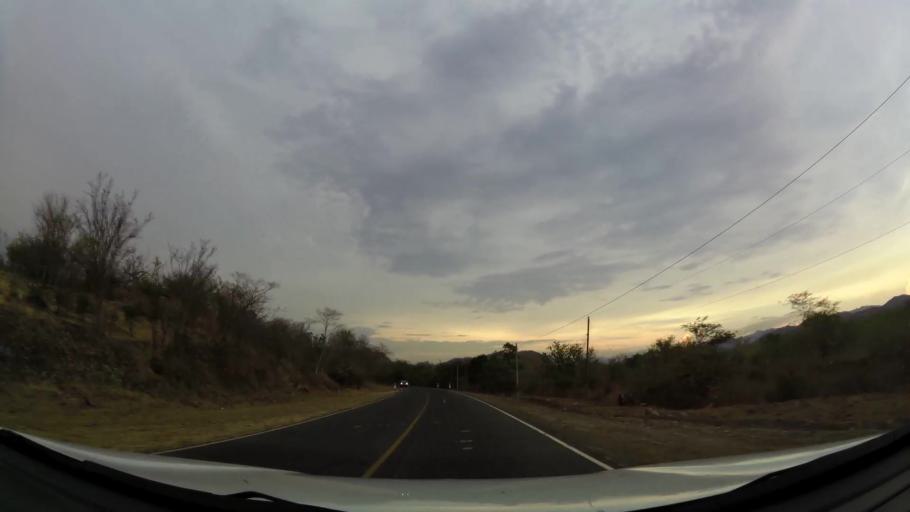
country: NI
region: Leon
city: La Jicaral
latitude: 12.7096
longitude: -86.3948
